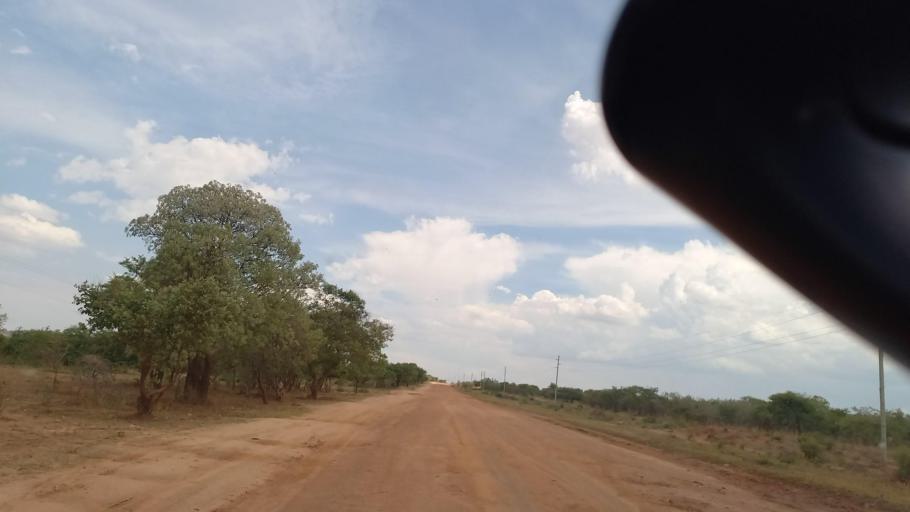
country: ZM
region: Lusaka
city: Kafue
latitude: -16.1399
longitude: 28.0527
